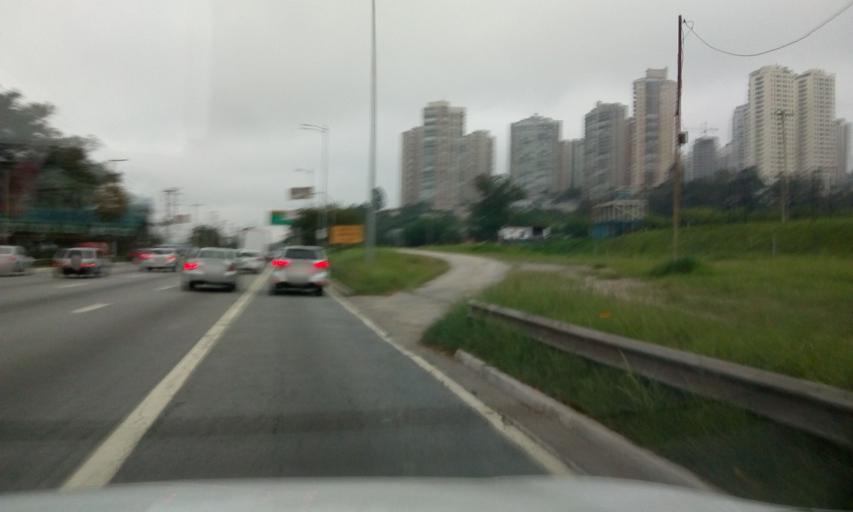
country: BR
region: Sao Paulo
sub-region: Taboao Da Serra
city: Taboao da Serra
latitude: -23.6268
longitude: -46.7137
